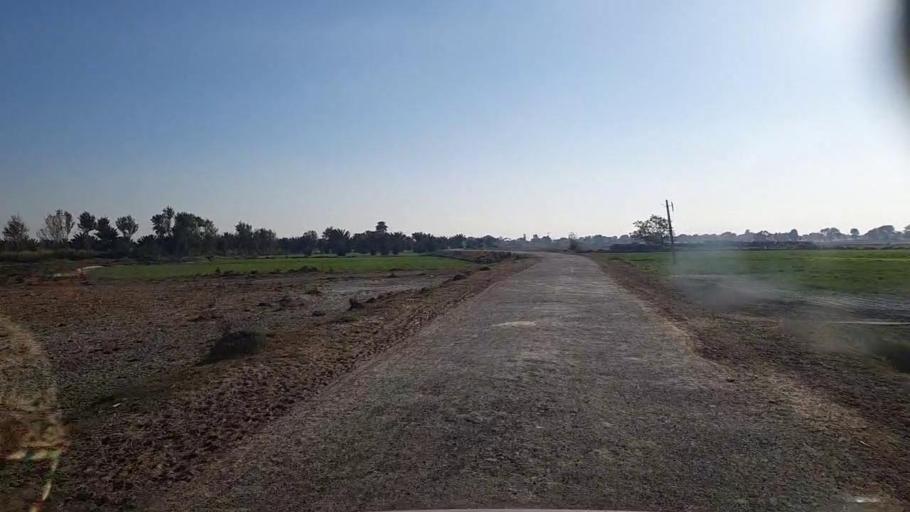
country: PK
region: Sindh
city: Khairpur
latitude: 28.0107
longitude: 69.7215
